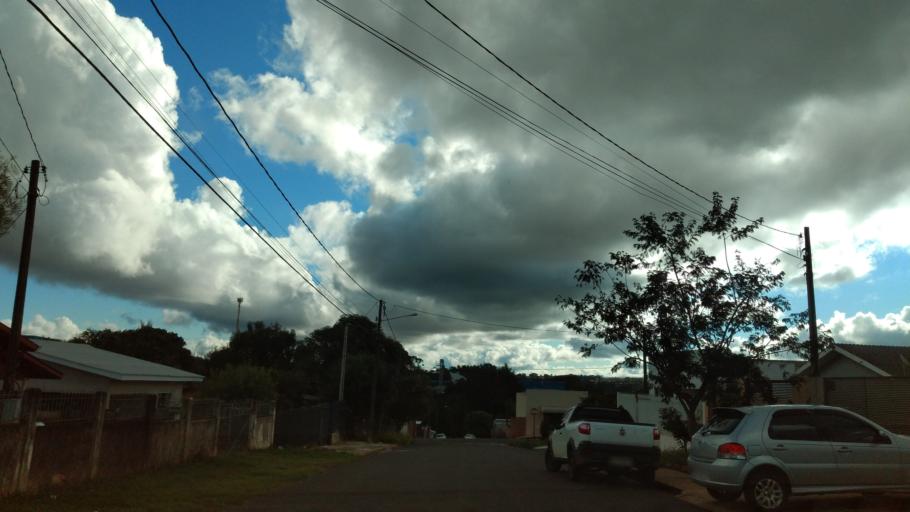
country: BR
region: Parana
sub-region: Guarapuava
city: Guarapuava
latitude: -25.3975
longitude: -51.4904
